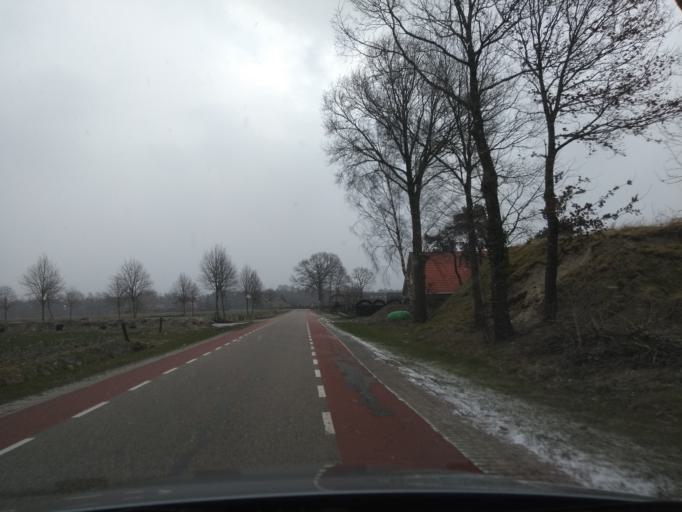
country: NL
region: Overijssel
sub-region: Gemeente Hof van Twente
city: Delden
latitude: 52.2224
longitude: 6.7032
